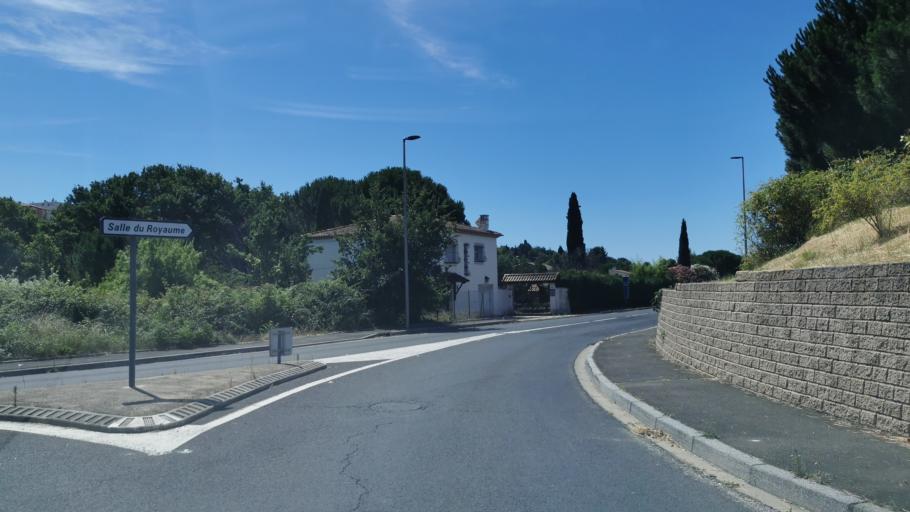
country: FR
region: Languedoc-Roussillon
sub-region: Departement de l'Herault
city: Beziers
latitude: 43.3608
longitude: 3.2123
